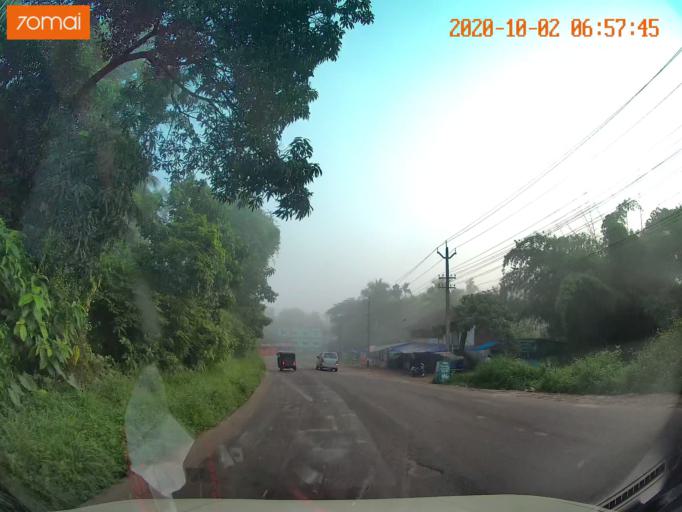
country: IN
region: Kerala
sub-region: Malappuram
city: Tirur
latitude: 10.8706
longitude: 76.0560
